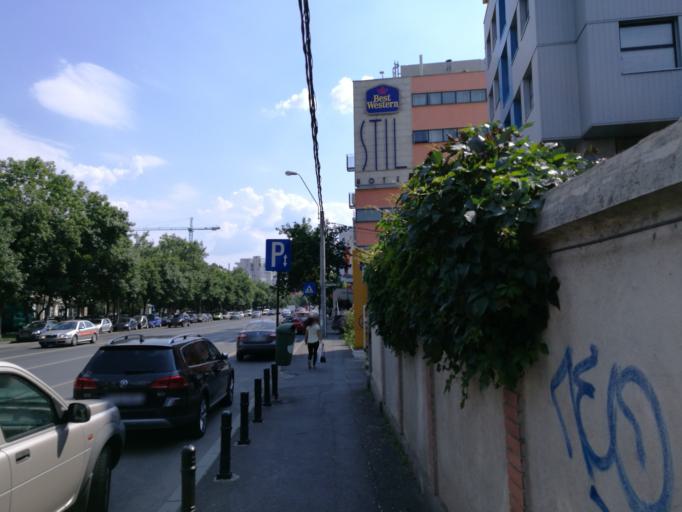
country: RO
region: Bucuresti
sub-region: Municipiul Bucuresti
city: Bucharest
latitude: 44.4819
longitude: 26.0921
